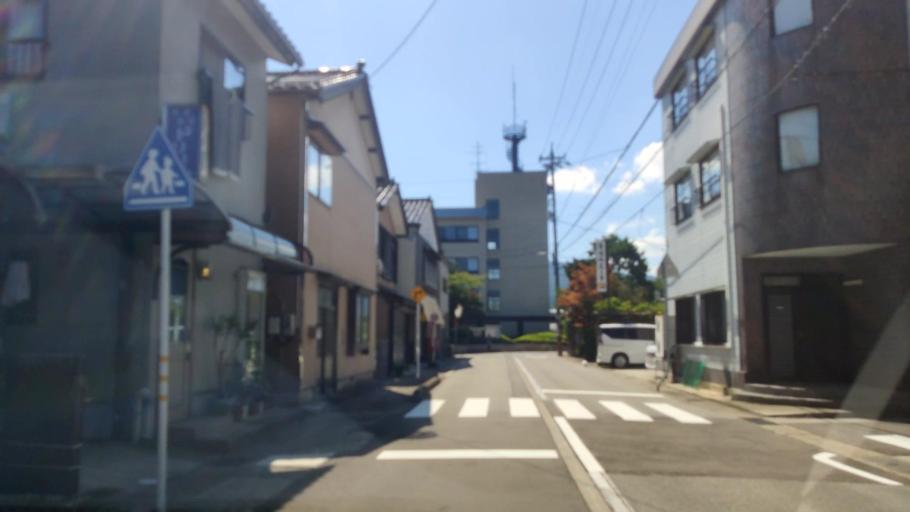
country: JP
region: Ishikawa
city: Nanao
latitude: 37.3927
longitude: 136.8954
